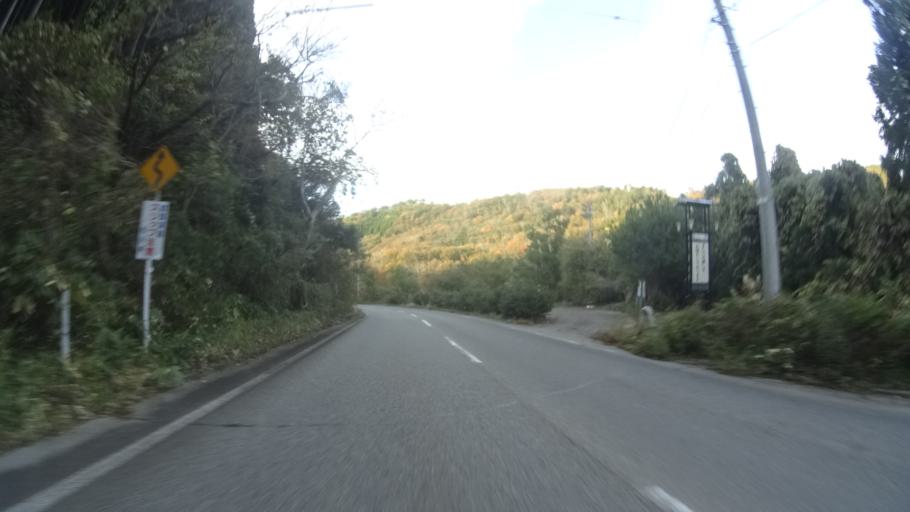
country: JP
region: Ishikawa
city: Nanao
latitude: 37.2146
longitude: 136.7065
